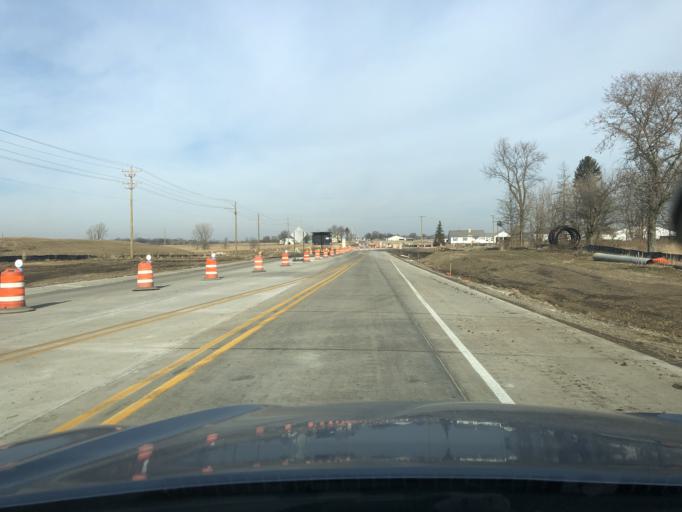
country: US
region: Illinois
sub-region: McHenry County
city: Marengo
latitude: 42.1805
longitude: -88.6179
